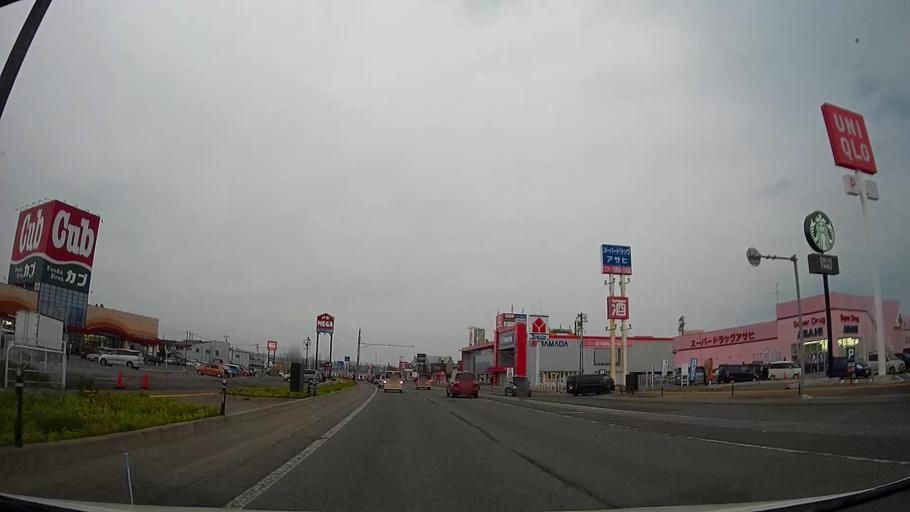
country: JP
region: Aomori
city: Aomori Shi
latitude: 40.8308
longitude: 140.7039
